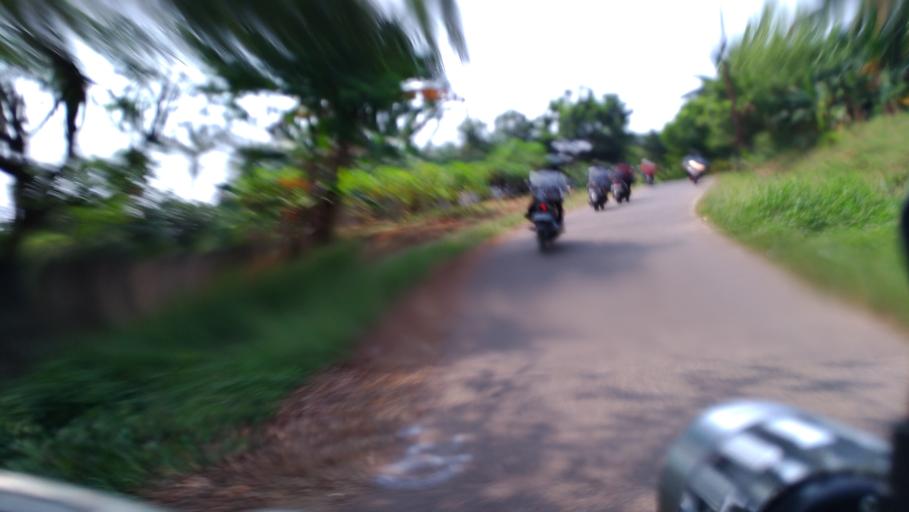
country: ID
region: West Java
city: Cileungsir
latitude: -6.3555
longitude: 106.8957
